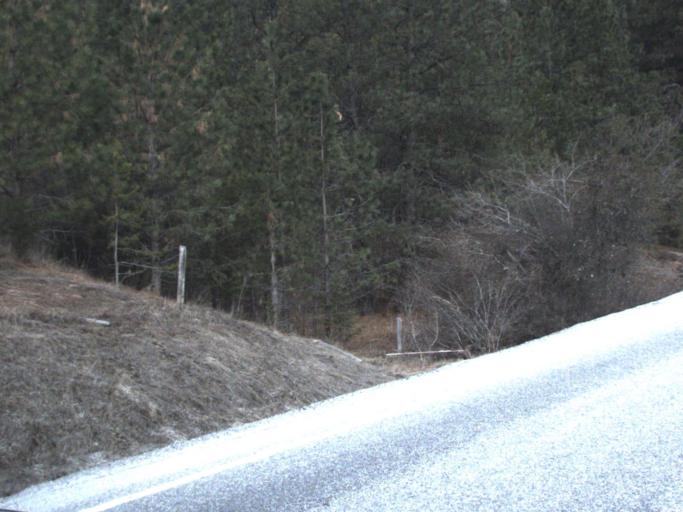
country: US
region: Washington
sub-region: Pend Oreille County
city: Newport
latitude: 48.4964
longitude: -117.2690
